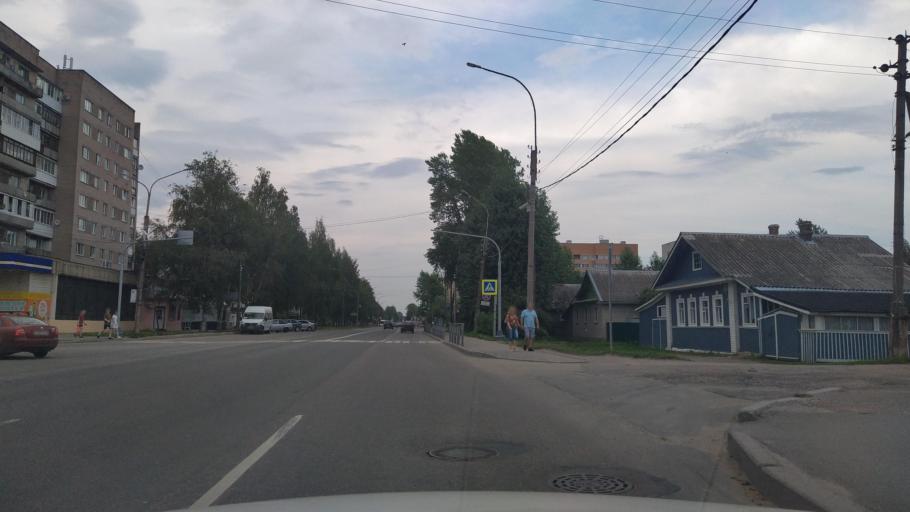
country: RU
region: Novgorod
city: Velikiy Novgorod
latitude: 58.5128
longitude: 31.2404
